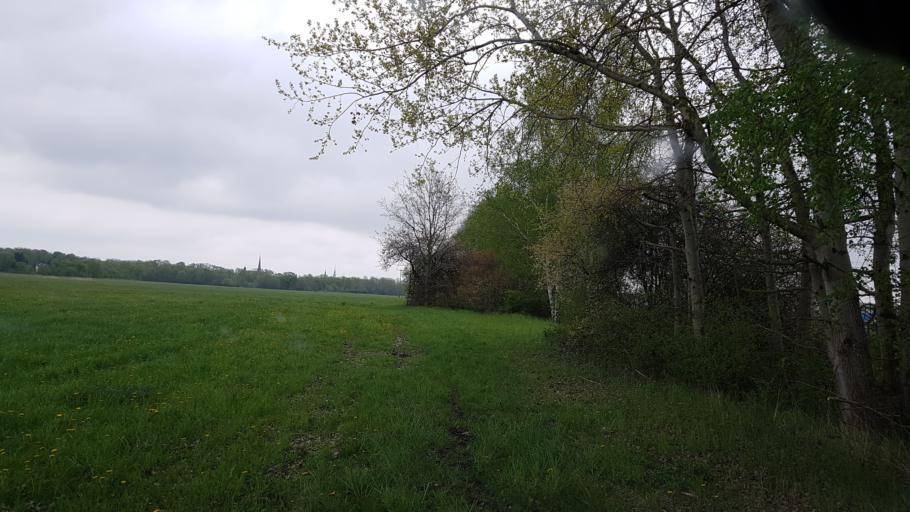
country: DE
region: Brandenburg
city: Doberlug-Kirchhain
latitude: 51.6071
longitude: 13.5298
